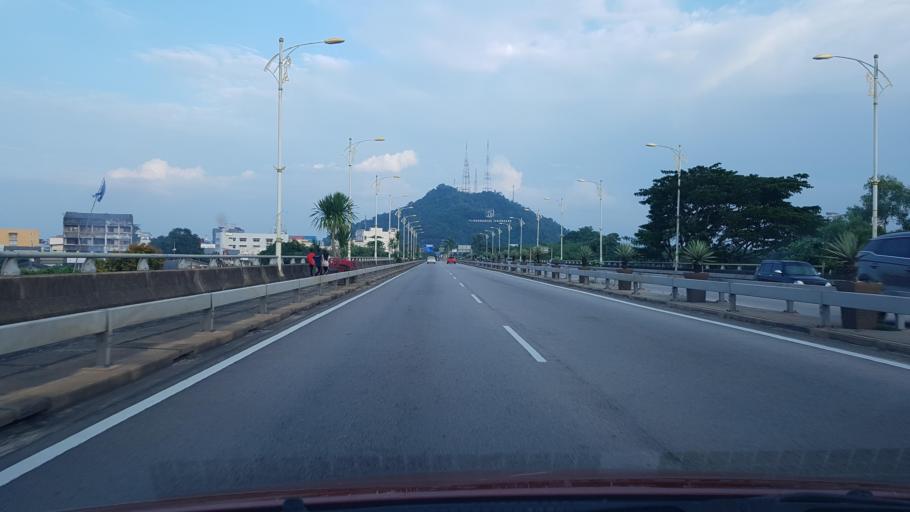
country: MY
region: Terengganu
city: Kuala Terengganu
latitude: 5.3203
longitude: 103.1271
